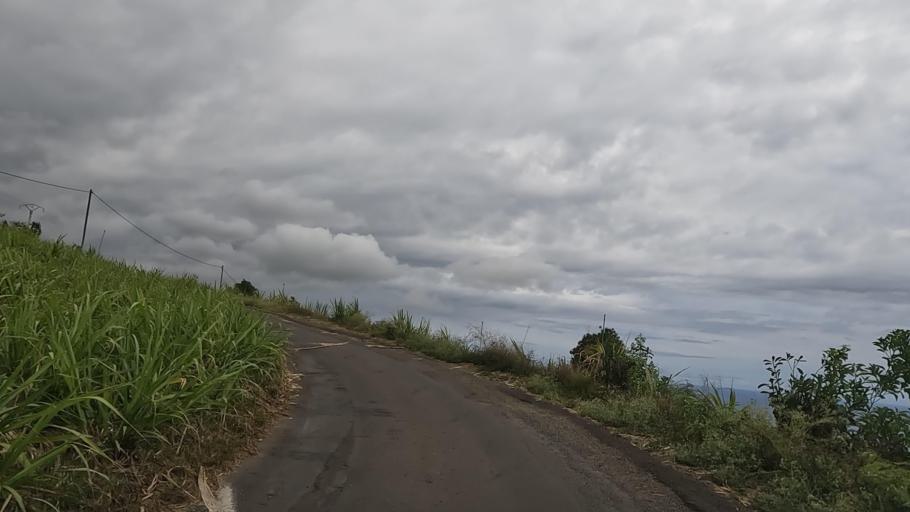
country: RE
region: Reunion
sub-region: Reunion
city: Petite-Ile
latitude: -21.3419
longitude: 55.5327
